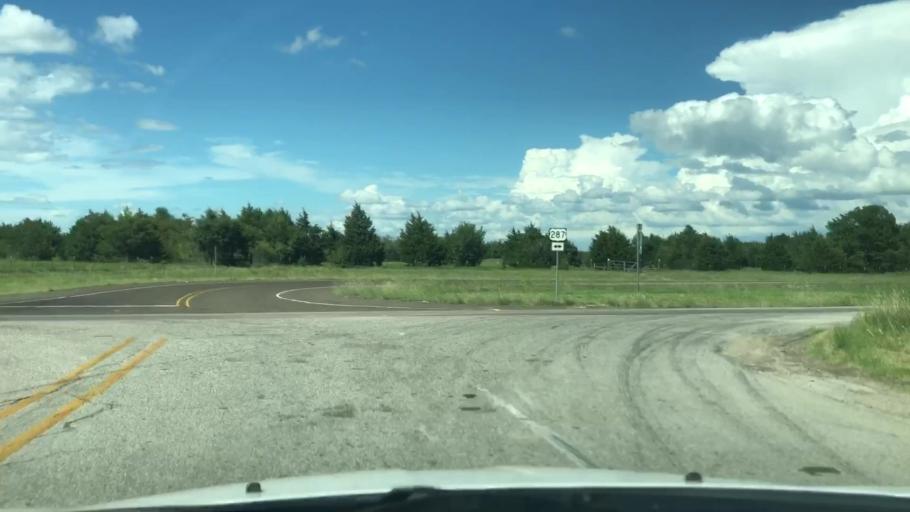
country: US
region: Texas
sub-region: Navarro County
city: Corsicana
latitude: 32.0364
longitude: -96.4016
